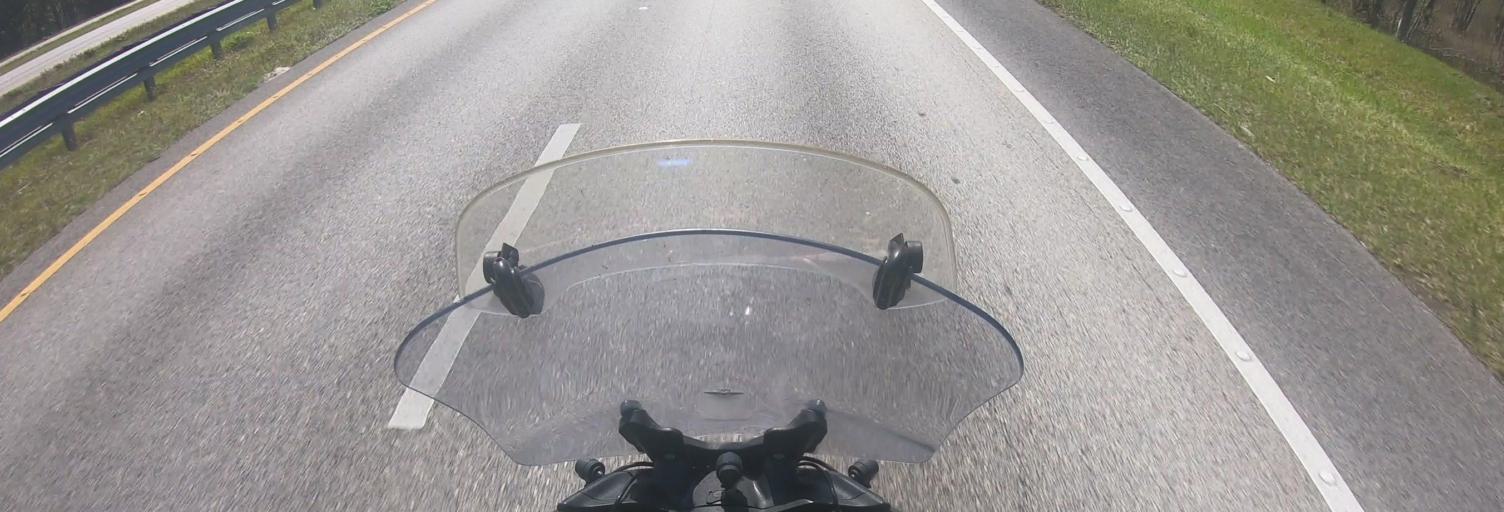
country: US
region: Florida
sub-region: Miami-Dade County
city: Kendall West
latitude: 25.7435
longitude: -80.4817
